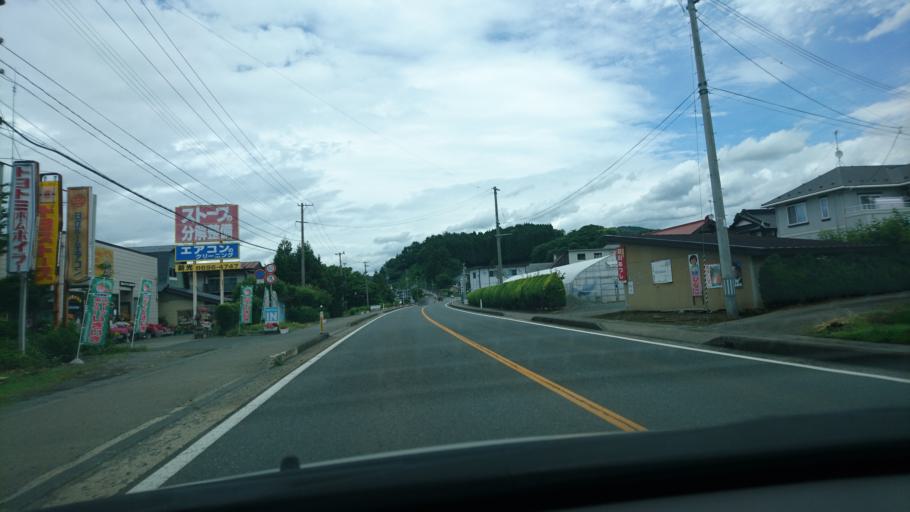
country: JP
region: Iwate
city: Morioka-shi
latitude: 39.6299
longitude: 141.1834
